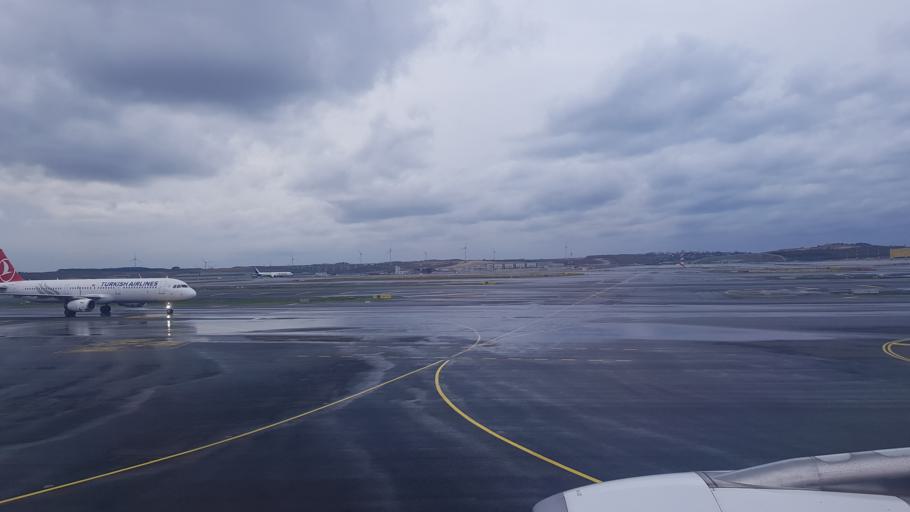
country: TR
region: Istanbul
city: Durusu
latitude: 41.2662
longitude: 28.7336
